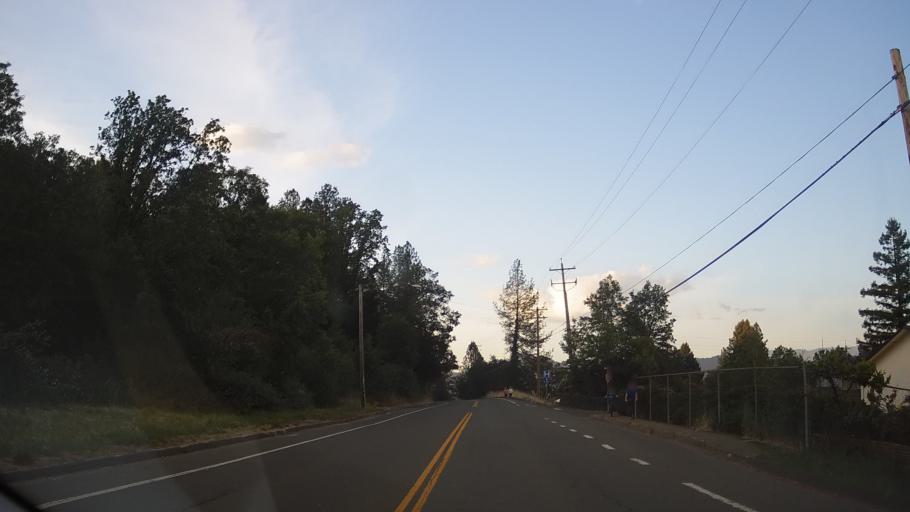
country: US
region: California
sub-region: Mendocino County
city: Willits
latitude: 39.3888
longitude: -123.3446
